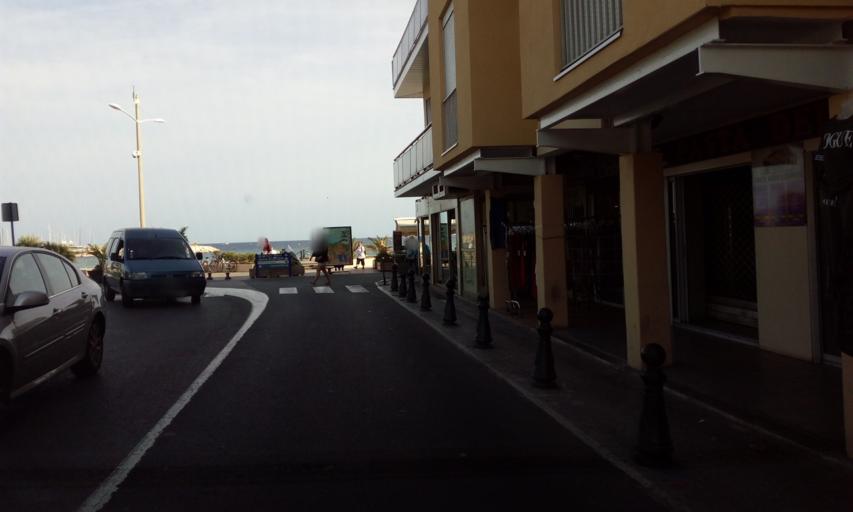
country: FR
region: Provence-Alpes-Cote d'Azur
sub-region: Departement du Var
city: Le Lavandou
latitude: 43.1364
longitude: 6.3670
